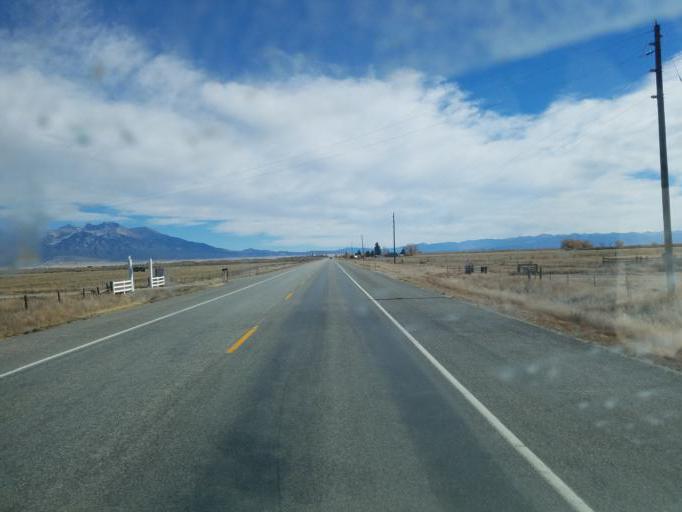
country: US
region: Colorado
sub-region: Alamosa County
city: Alamosa East
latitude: 37.4739
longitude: -105.7640
